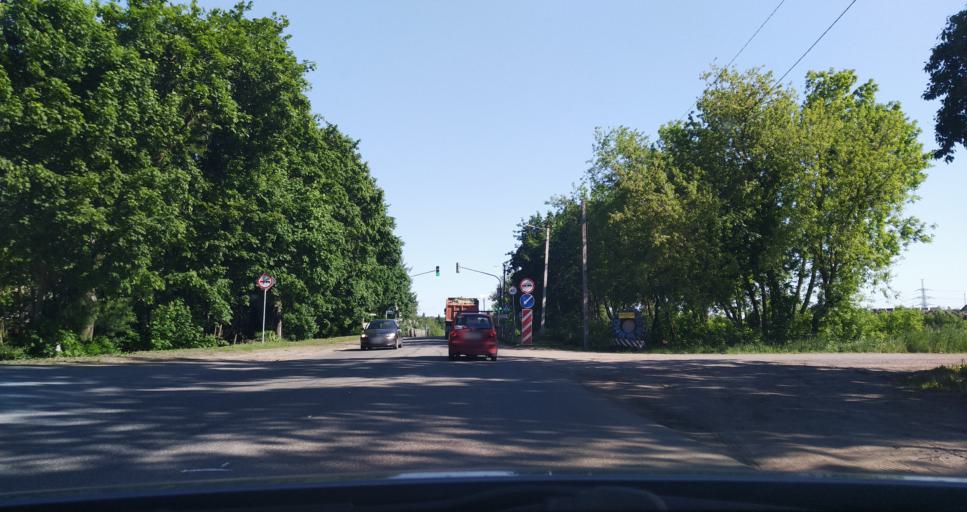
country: RU
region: Leningrad
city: Taytsy
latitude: 59.6974
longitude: 30.1035
